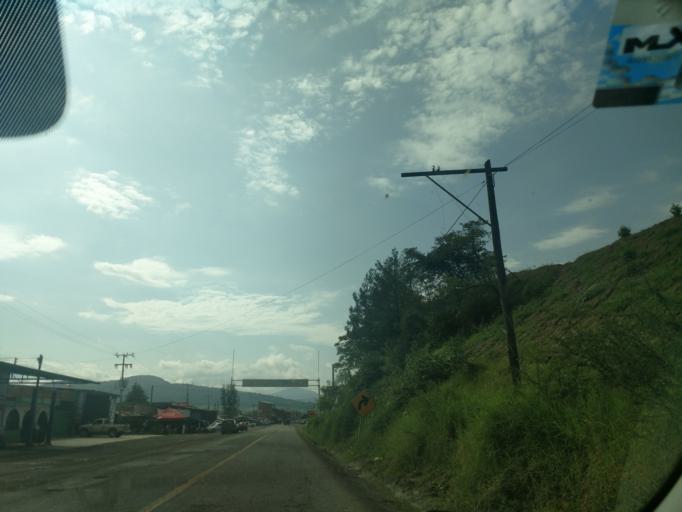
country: MX
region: Jalisco
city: El Salto
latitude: 20.4218
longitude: -104.5007
